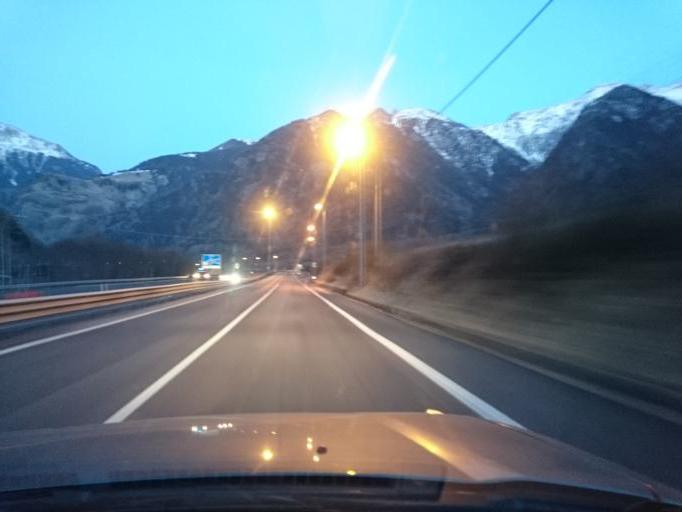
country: IT
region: Lombardy
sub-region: Provincia di Sondrio
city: Sondalo
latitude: 46.3253
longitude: 10.3323
